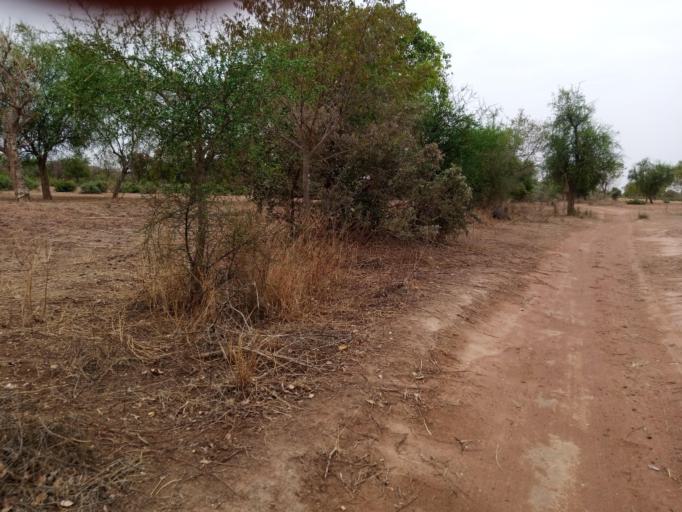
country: BF
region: Boucle du Mouhoun
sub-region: Province de la Kossi
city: Nouna
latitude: 12.8348
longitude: -4.0772
